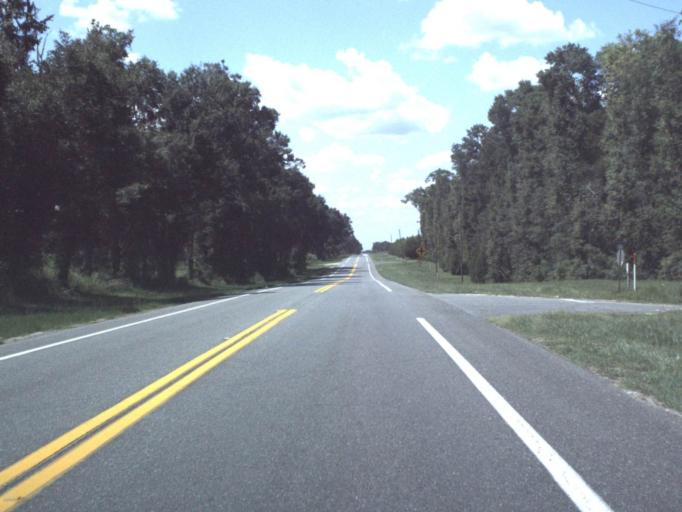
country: US
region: Florida
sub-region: Alachua County
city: High Springs
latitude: 29.9845
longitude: -82.7100
